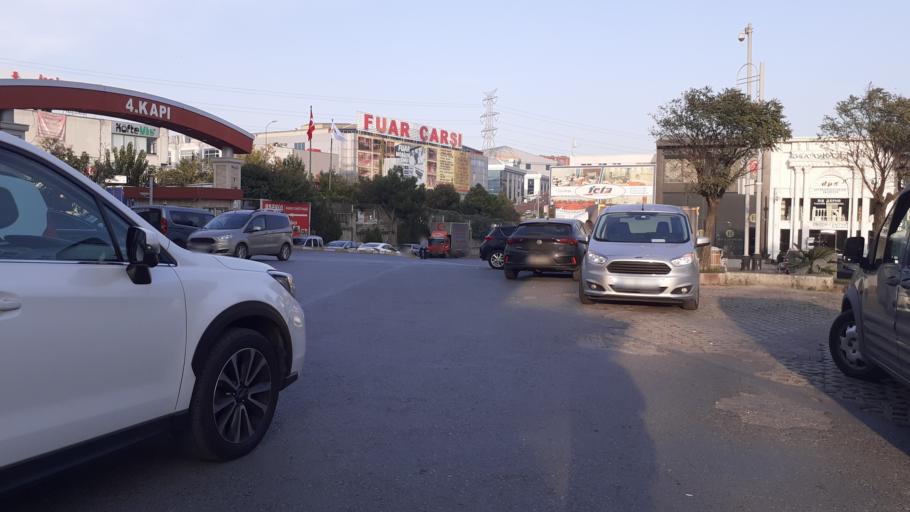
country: TR
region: Istanbul
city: Basaksehir
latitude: 41.0672
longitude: 28.7942
